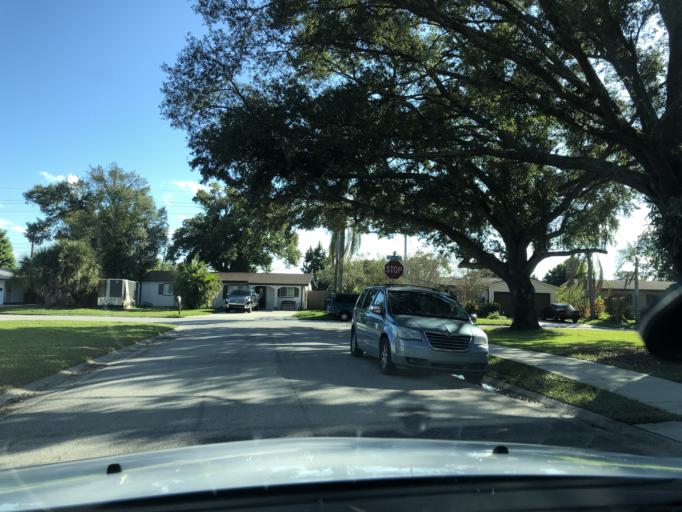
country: US
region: Florida
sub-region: Orange County
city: Oak Ridge
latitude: 28.4735
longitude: -81.4321
